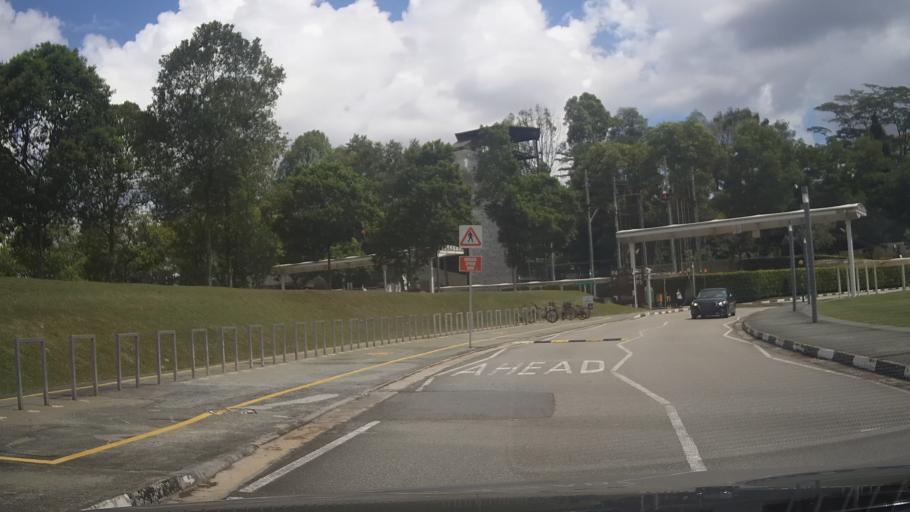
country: MY
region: Johor
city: Johor Bahru
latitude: 1.4452
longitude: 103.7836
